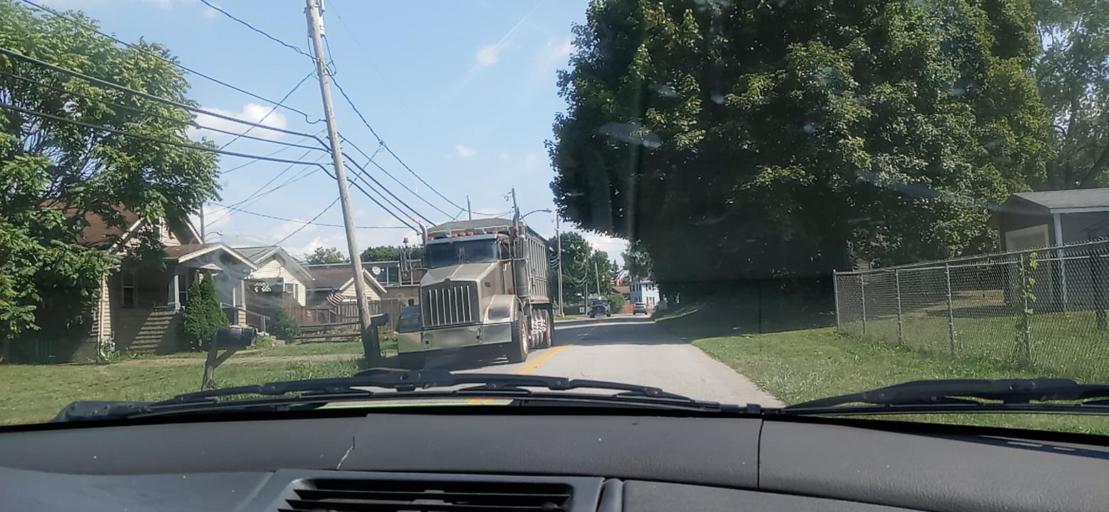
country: US
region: Ohio
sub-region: Summit County
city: Barberton
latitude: 41.0386
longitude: -81.5774
